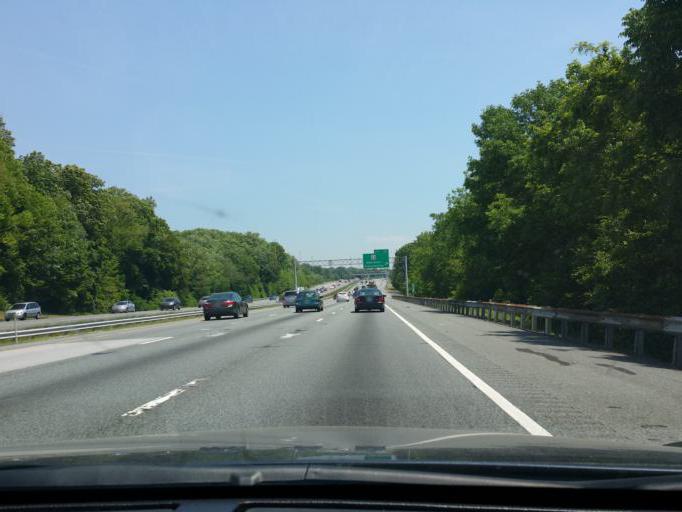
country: US
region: Maryland
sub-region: Harford County
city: Aberdeen
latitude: 39.5172
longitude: -76.2022
